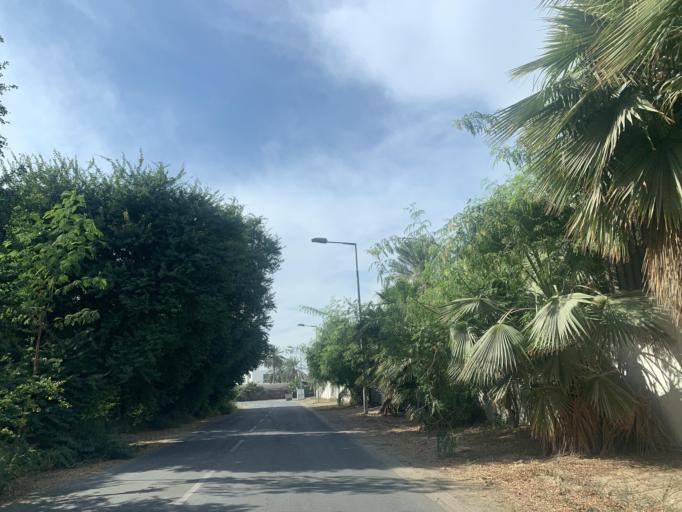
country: BH
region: Central Governorate
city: Madinat Hamad
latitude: 26.1257
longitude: 50.4725
